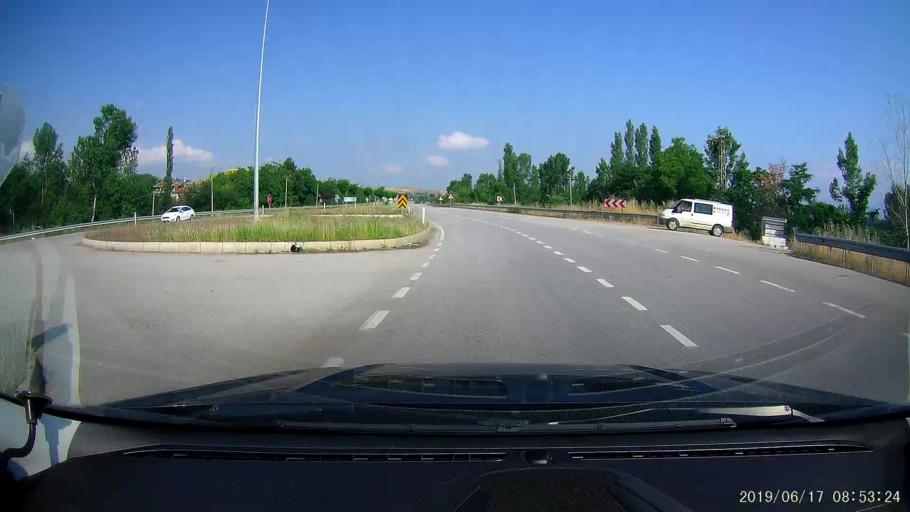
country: TR
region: Tokat
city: Erbaa
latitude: 40.7096
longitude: 36.4820
